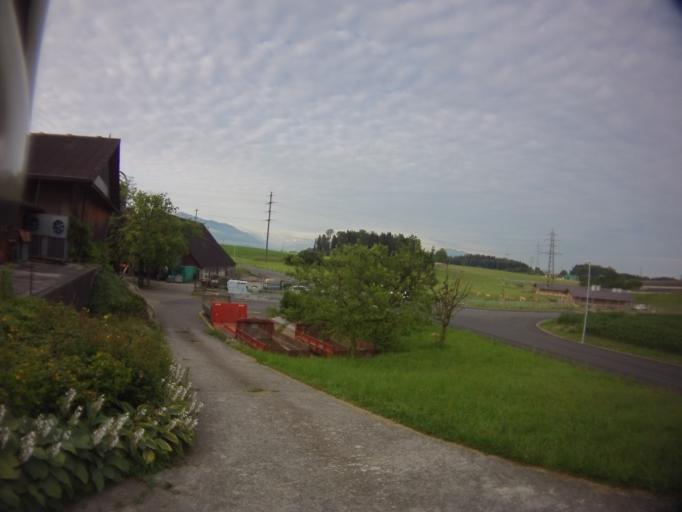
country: CH
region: Zug
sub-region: Zug
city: Steinhausen
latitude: 47.2062
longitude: 8.4705
